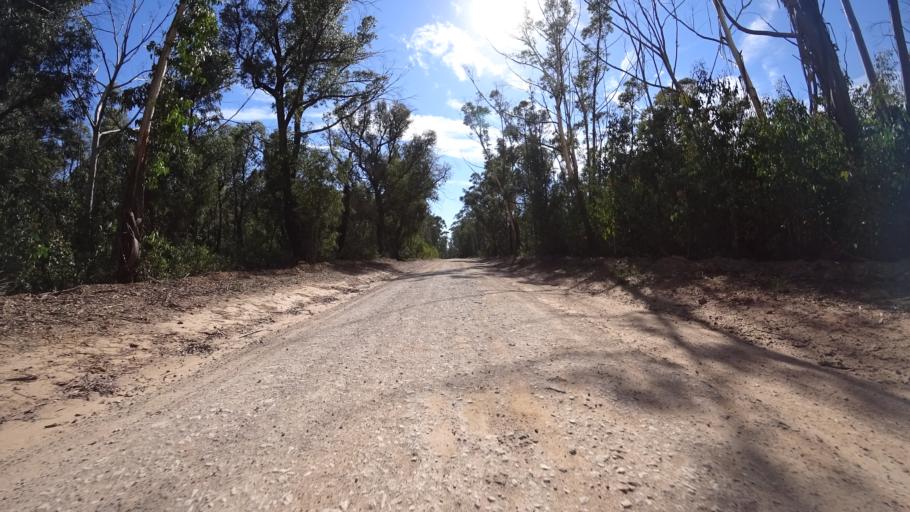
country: AU
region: New South Wales
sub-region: Lithgow
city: Lithgow
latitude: -33.4295
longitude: 150.1971
